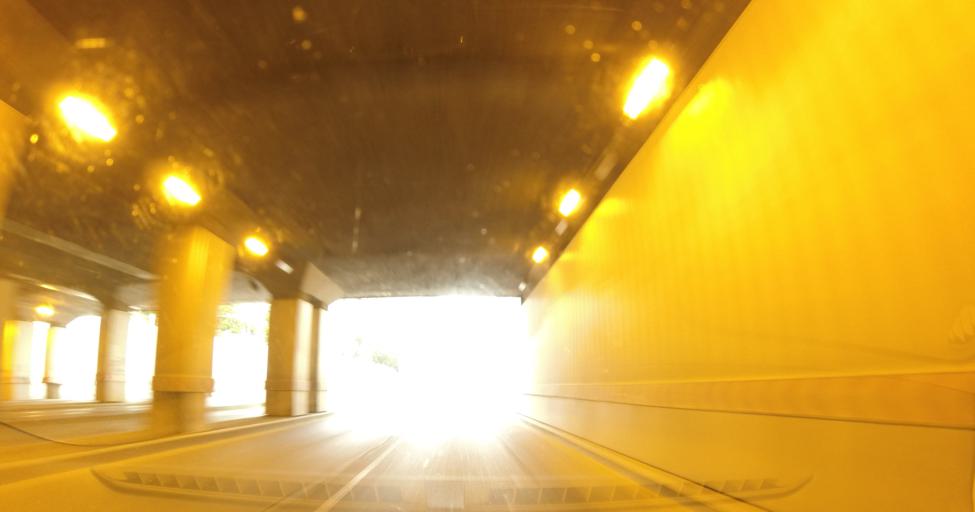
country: RO
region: Bucuresti
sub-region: Municipiul Bucuresti
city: Bucuresti
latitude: 44.4518
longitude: 26.0843
